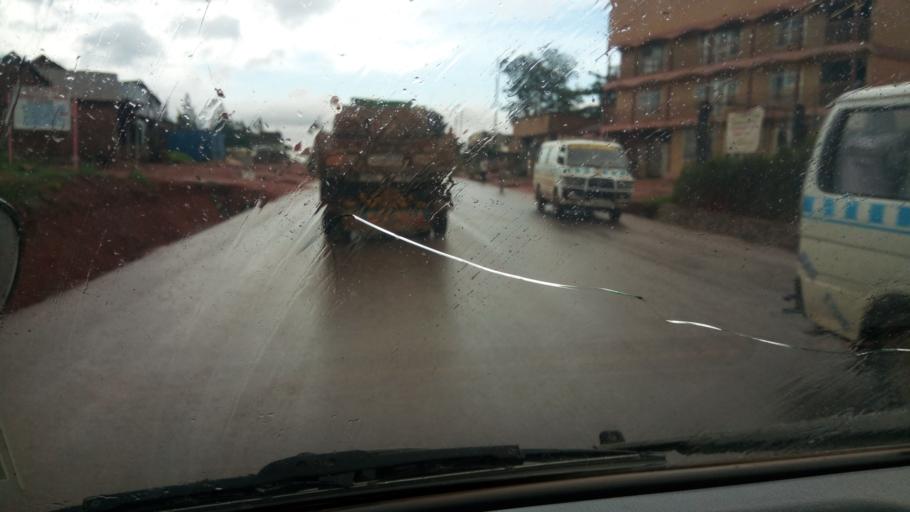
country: UG
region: Central Region
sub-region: Wakiso District
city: Wakiso
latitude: 0.3965
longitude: 32.4926
